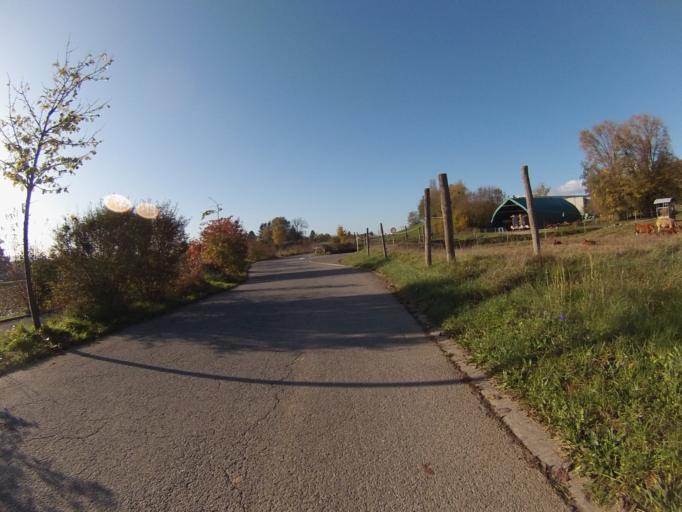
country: CH
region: Geneva
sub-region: Geneva
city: Meyrin
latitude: 46.2395
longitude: 6.0689
